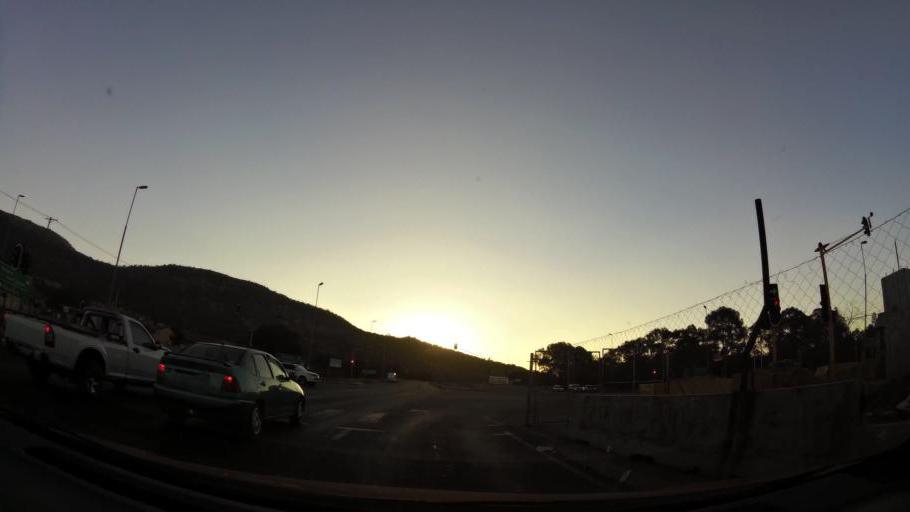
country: ZA
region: North-West
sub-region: Bojanala Platinum District Municipality
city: Rustenburg
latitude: -25.6403
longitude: 27.1999
